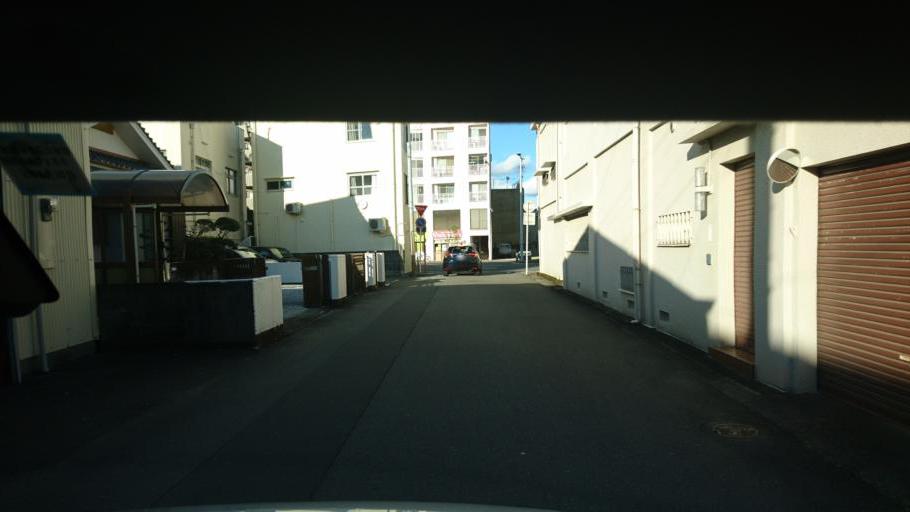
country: JP
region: Miyazaki
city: Miyazaki-shi
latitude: 31.8961
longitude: 131.4201
